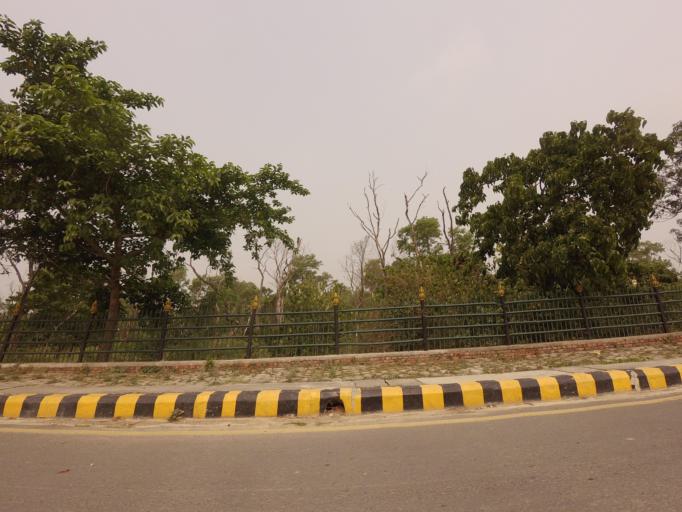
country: IN
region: Uttar Pradesh
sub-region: Maharajganj
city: Nautanwa
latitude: 27.4767
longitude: 83.2839
